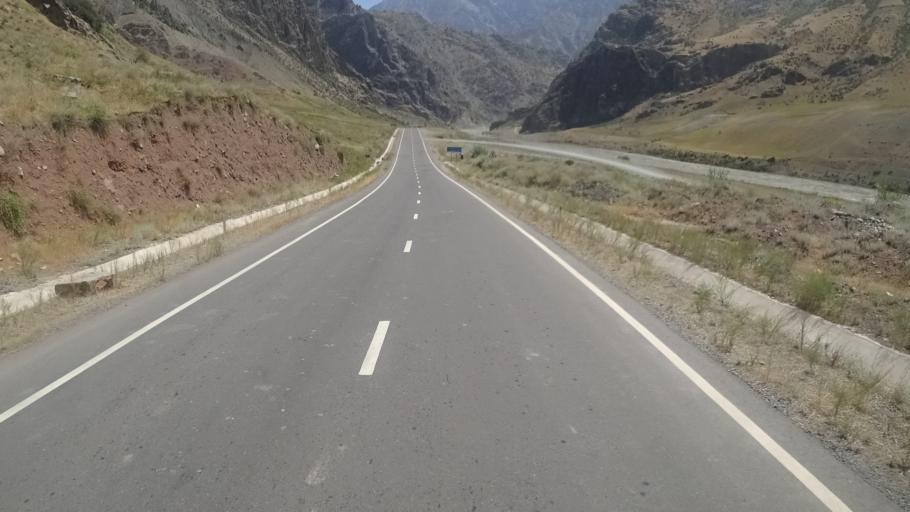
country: AF
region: Badakhshan
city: Deh Khwahan
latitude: 37.9411
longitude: 70.2306
